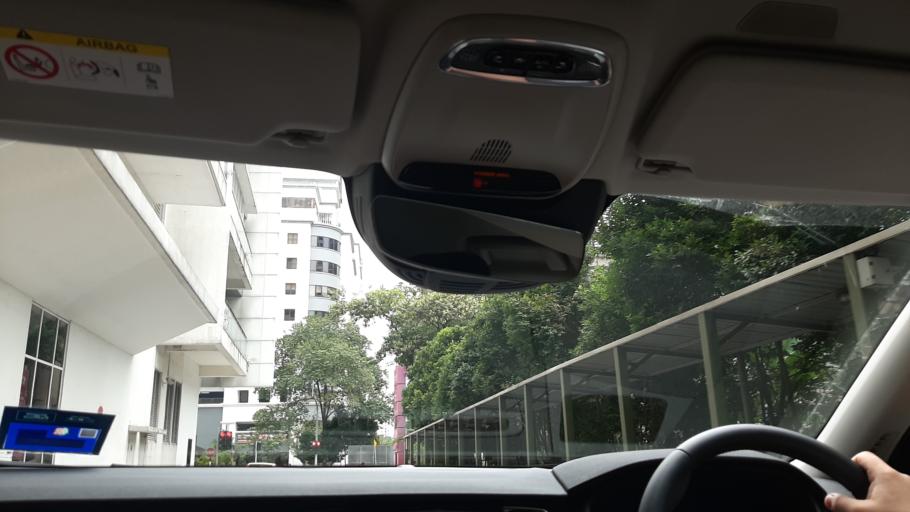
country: MY
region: Kuala Lumpur
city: Kuala Lumpur
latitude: 3.1657
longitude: 101.6533
